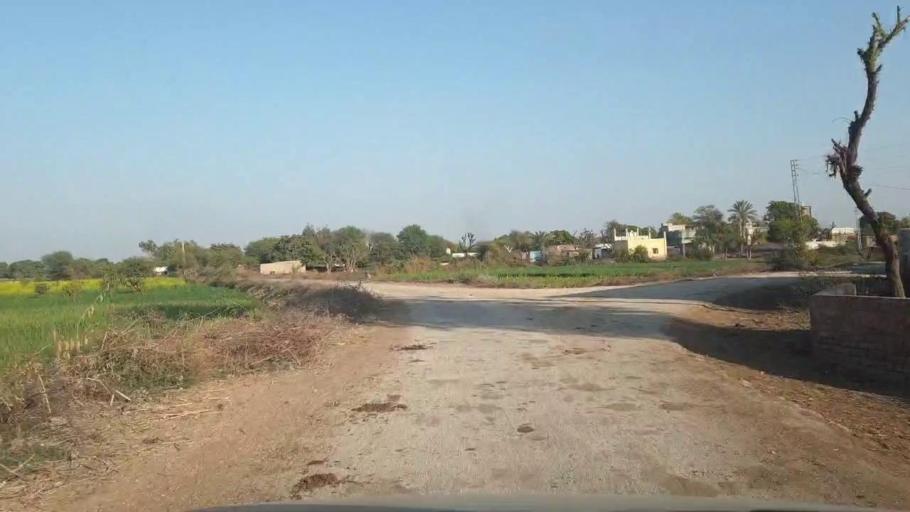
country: PK
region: Sindh
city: Chambar
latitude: 25.2579
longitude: 68.8952
